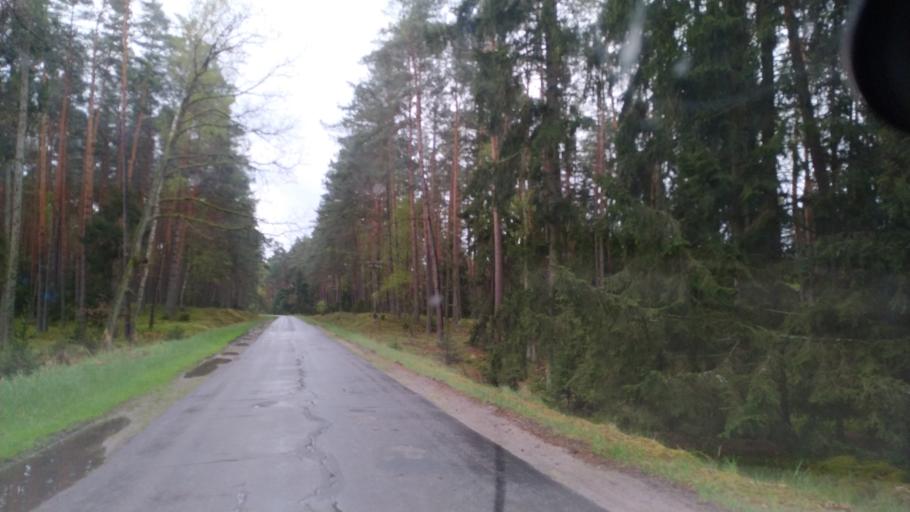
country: PL
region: Pomeranian Voivodeship
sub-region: Powiat starogardzki
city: Osiek
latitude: 53.6581
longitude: 18.4863
